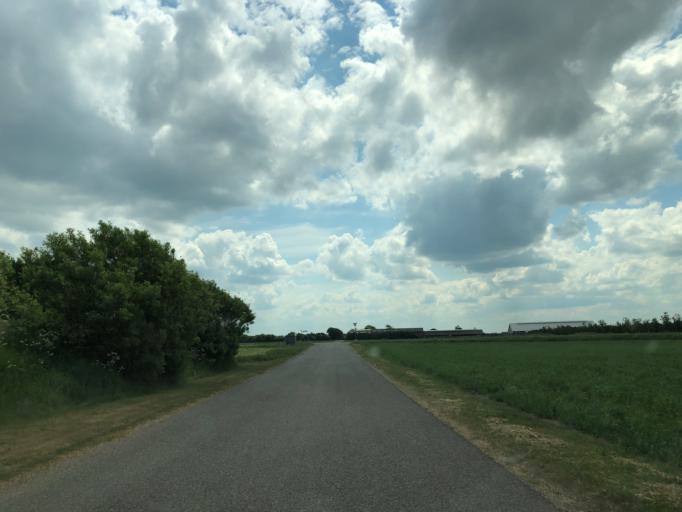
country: DK
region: Central Jutland
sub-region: Holstebro Kommune
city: Ulfborg
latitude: 56.3411
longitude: 8.3198
